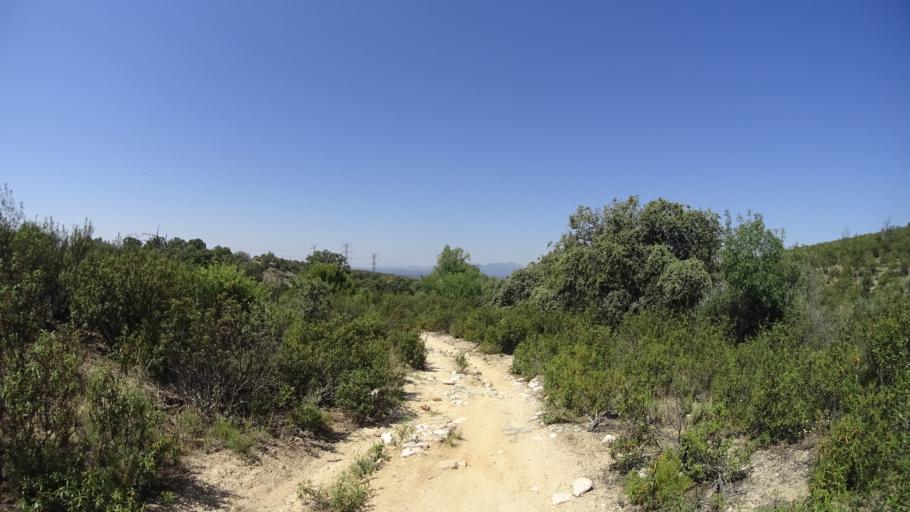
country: ES
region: Madrid
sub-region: Provincia de Madrid
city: Moralzarzal
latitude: 40.6354
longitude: -3.9529
